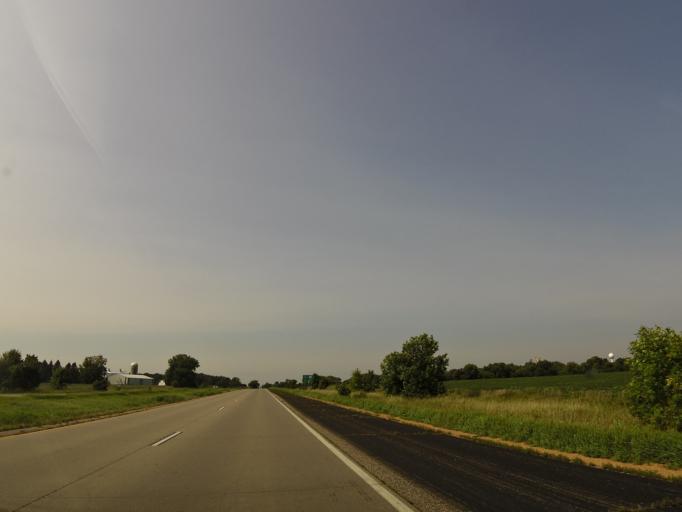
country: US
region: Minnesota
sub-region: Carver County
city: Cologne
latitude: 44.7698
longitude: -93.7695
